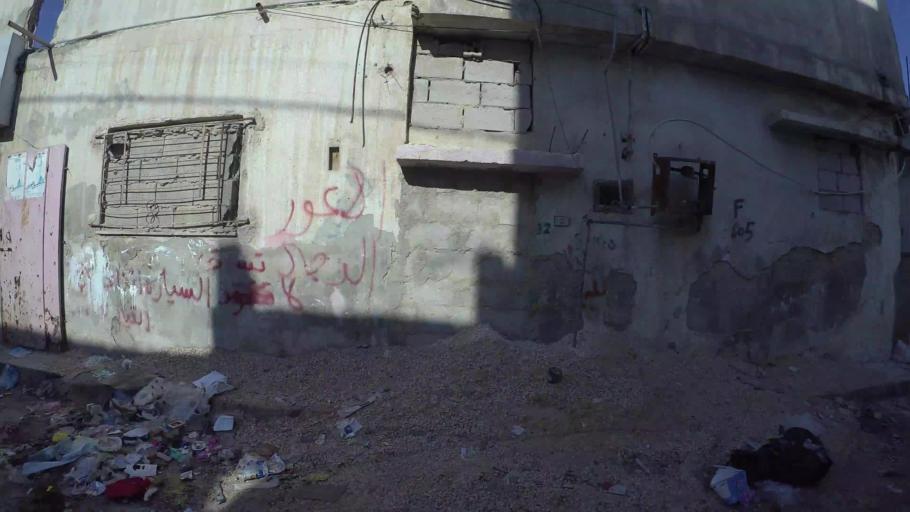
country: JO
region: Amman
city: Al Jubayhah
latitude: 32.0754
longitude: 35.8513
